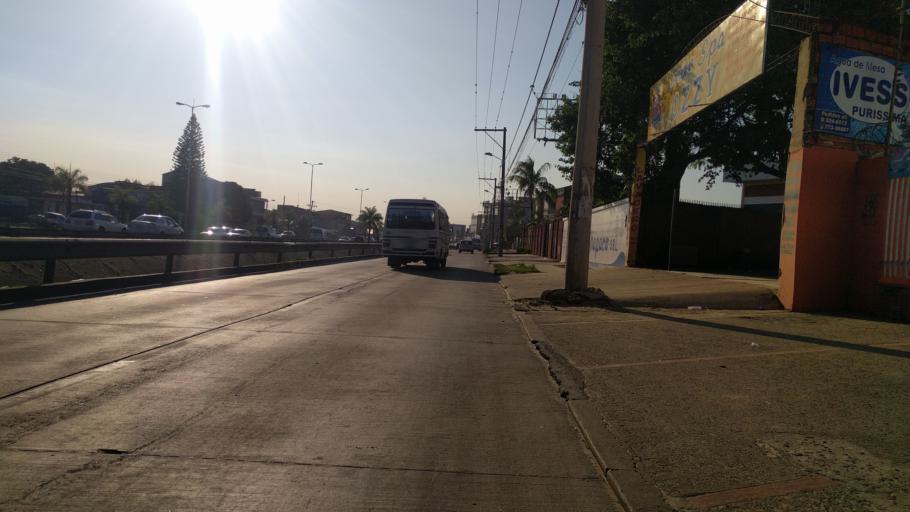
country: BO
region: Santa Cruz
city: Santa Cruz de la Sierra
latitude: -17.7985
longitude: -63.1730
